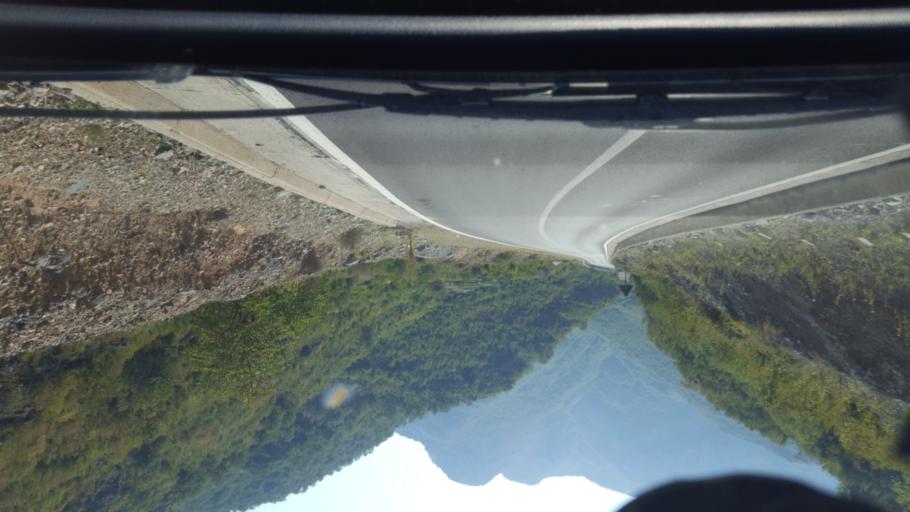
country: AL
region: Shkoder
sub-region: Rrethi i Malesia e Madhe
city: Kastrat
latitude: 42.4340
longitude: 19.5355
